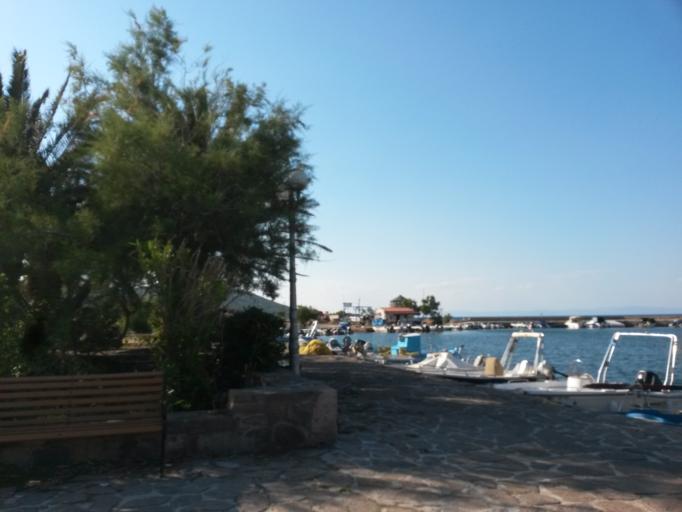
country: GR
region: North Aegean
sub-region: Nomos Lesvou
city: Pamfylla
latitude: 39.1814
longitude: 26.4993
